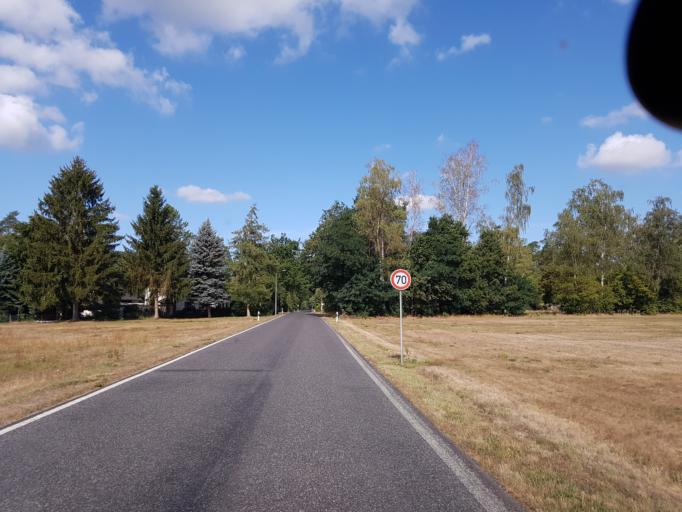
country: DE
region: Brandenburg
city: Sonnewalde
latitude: 51.7374
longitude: 13.6246
